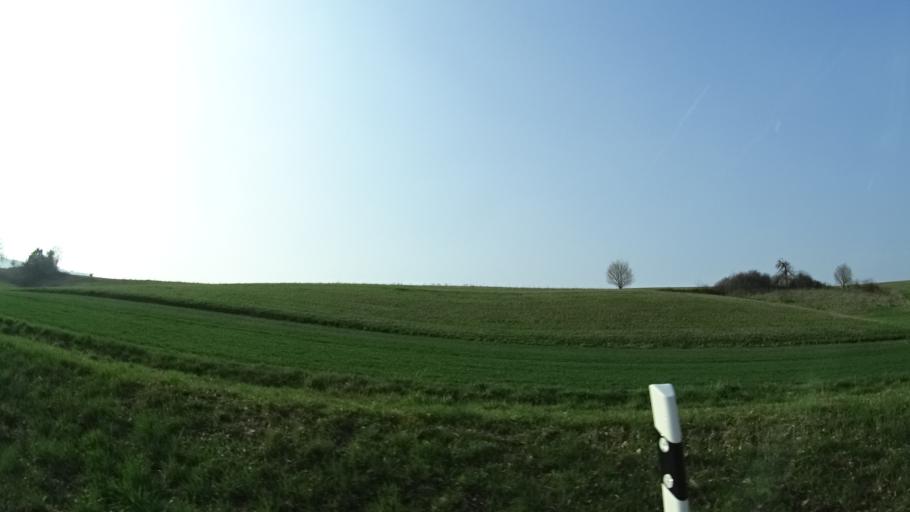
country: DE
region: Rheinland-Pfalz
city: Oberstaufenbach
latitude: 49.5244
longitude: 7.5131
